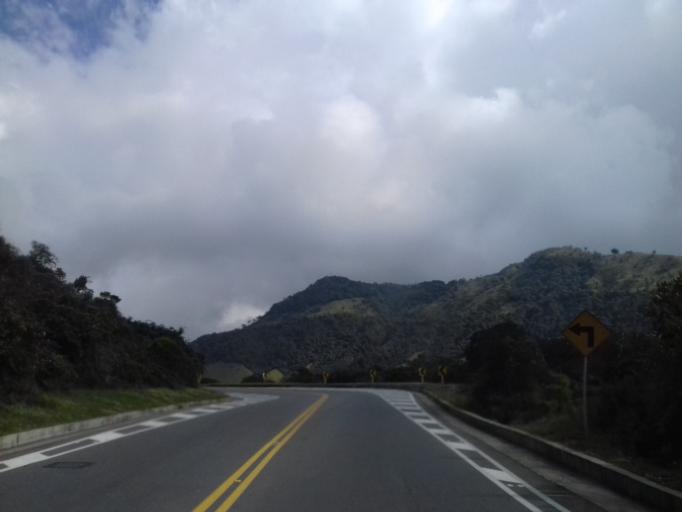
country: CO
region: Caldas
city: Villamaria
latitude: 5.0141
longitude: -75.3431
